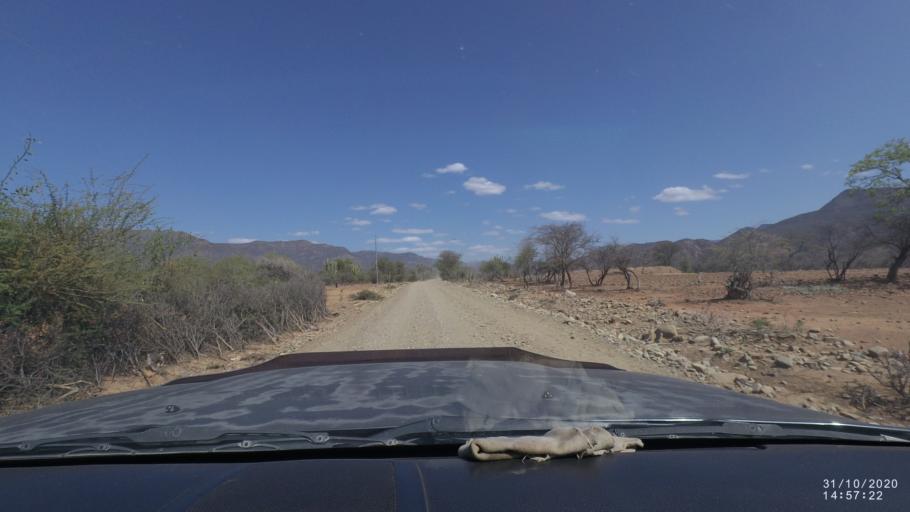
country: BO
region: Cochabamba
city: Aiquile
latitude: -18.2429
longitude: -64.8439
